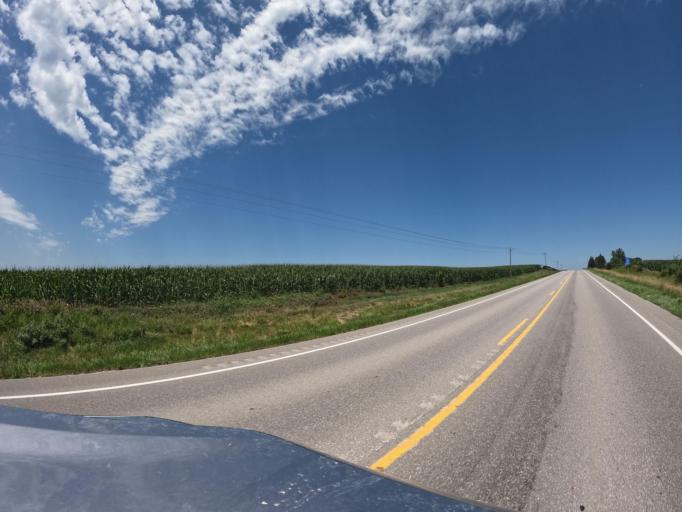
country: US
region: Iowa
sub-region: Keokuk County
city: Sigourney
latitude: 41.4126
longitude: -92.3545
